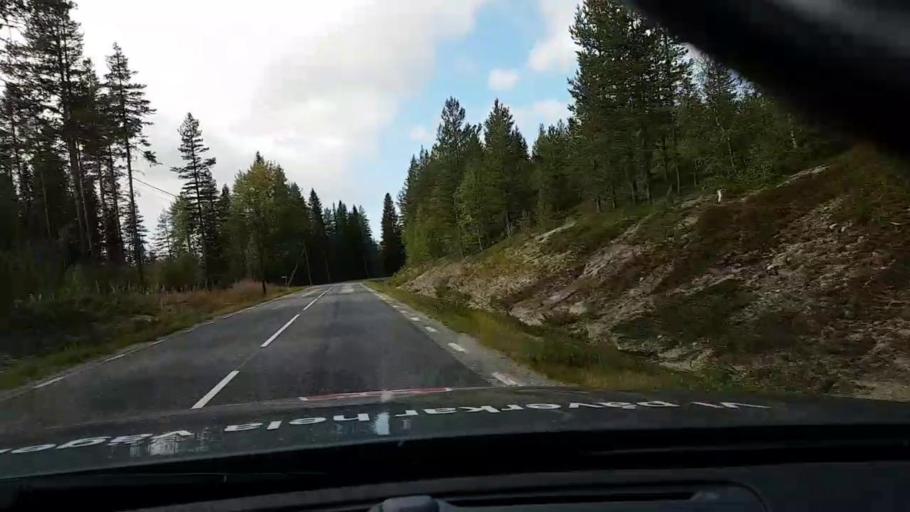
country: SE
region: Vaesterbotten
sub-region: Asele Kommun
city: Asele
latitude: 63.7943
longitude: 17.5706
